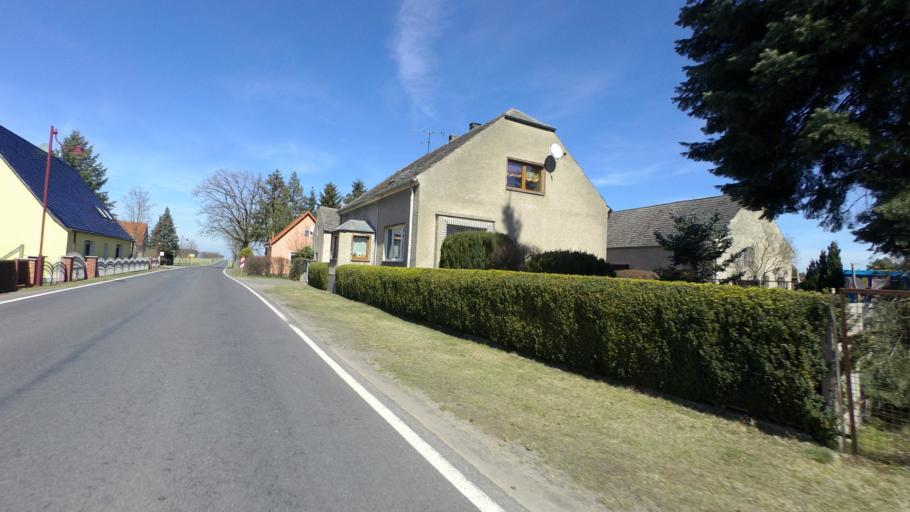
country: DE
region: Brandenburg
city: Munchehofe
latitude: 52.1634
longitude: 13.9208
